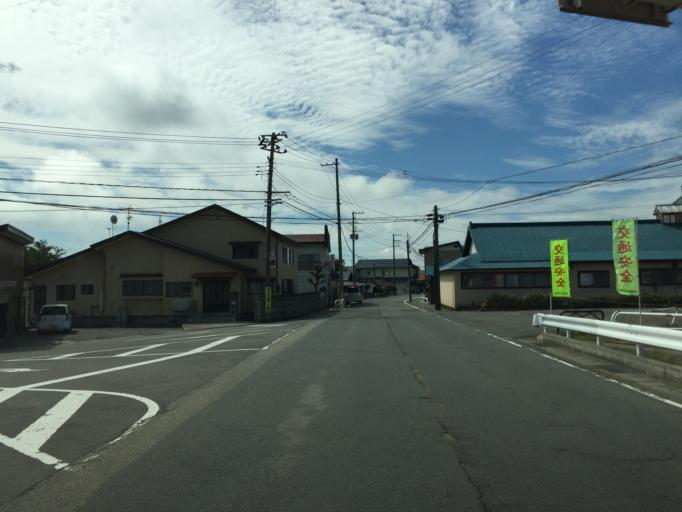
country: JP
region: Fukushima
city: Inawashiro
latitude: 37.5597
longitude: 139.9875
